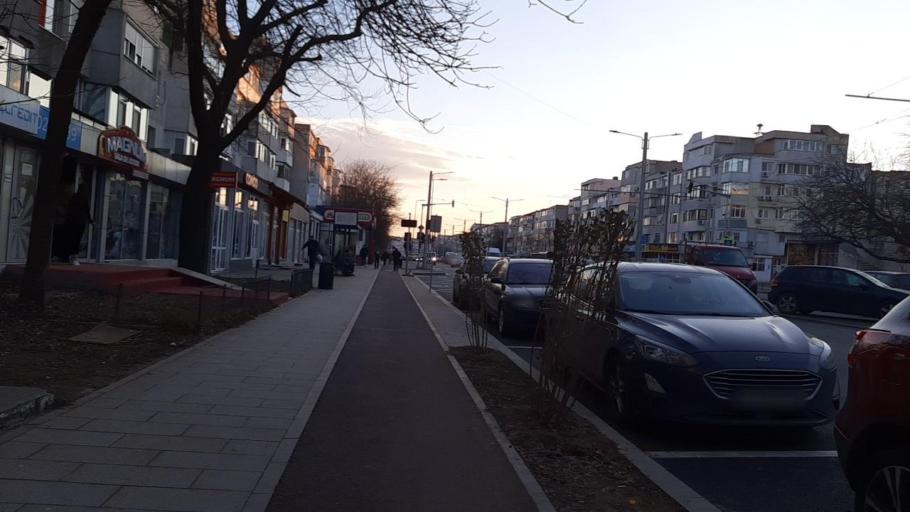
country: RO
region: Galati
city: Galati
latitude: 45.4453
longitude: 28.0235
